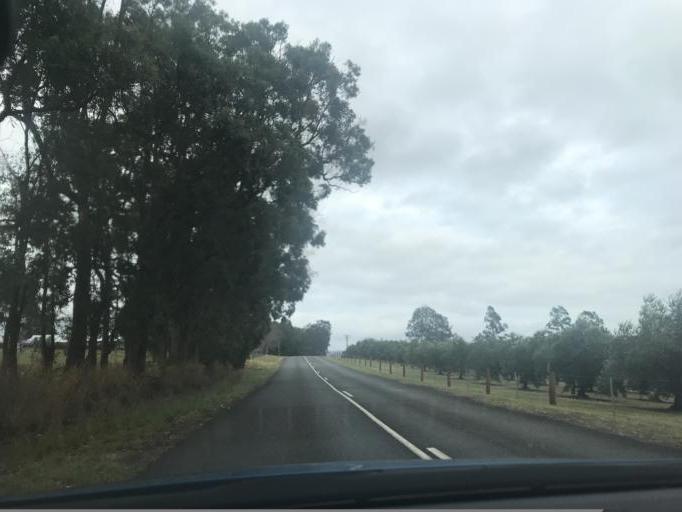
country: AU
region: New South Wales
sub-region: Cessnock
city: Cessnock
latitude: -32.8133
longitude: 151.3222
